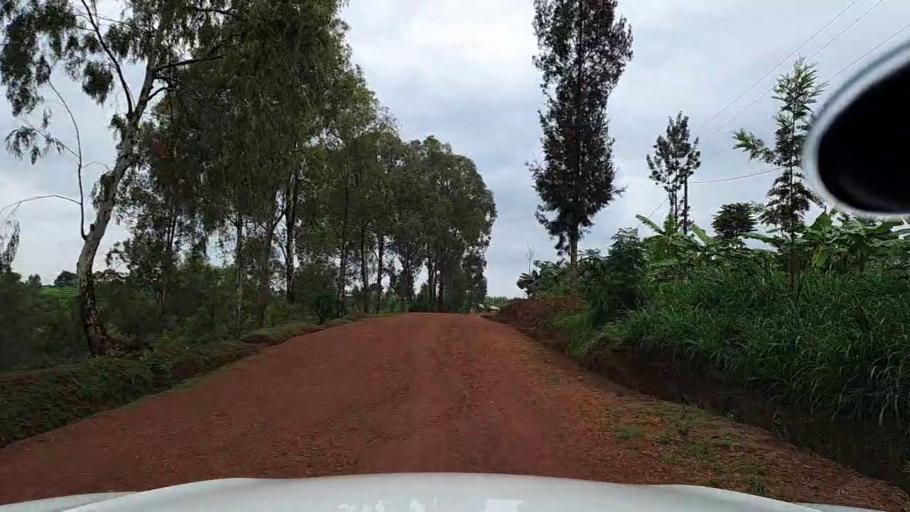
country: RW
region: Kigali
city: Kigali
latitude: -1.9013
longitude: 29.8972
